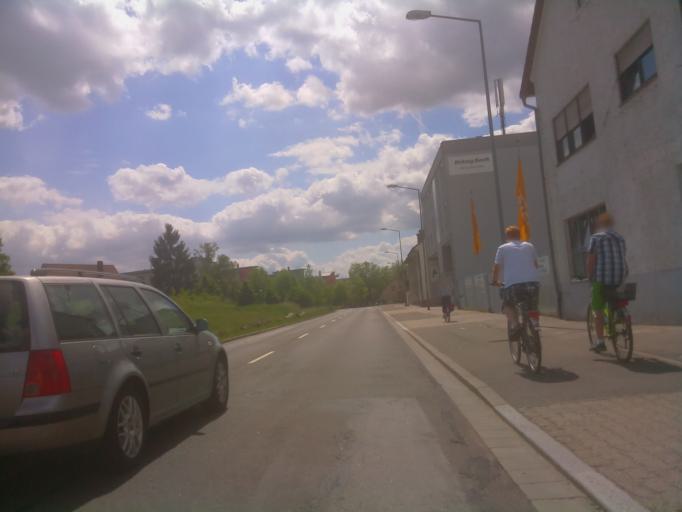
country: DE
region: Rheinland-Pfalz
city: Speyer
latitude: 49.3236
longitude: 8.4467
